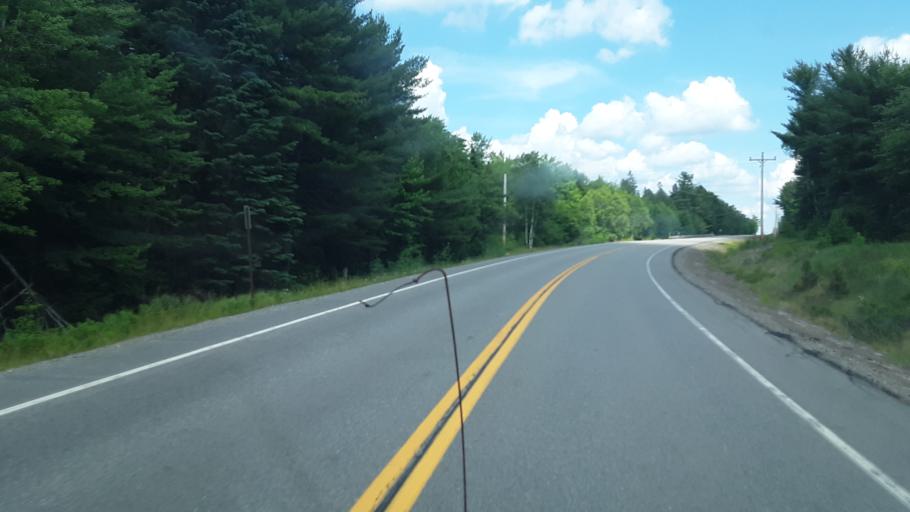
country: US
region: Maine
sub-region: Washington County
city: Machias
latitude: 45.0000
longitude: -67.6022
